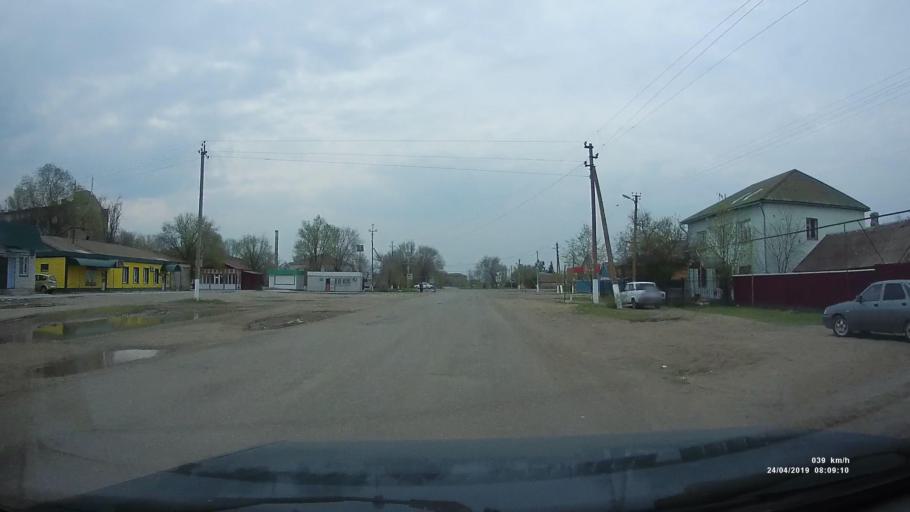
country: RU
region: Kalmykiya
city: Priyutnoye
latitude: 46.0967
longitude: 43.5050
